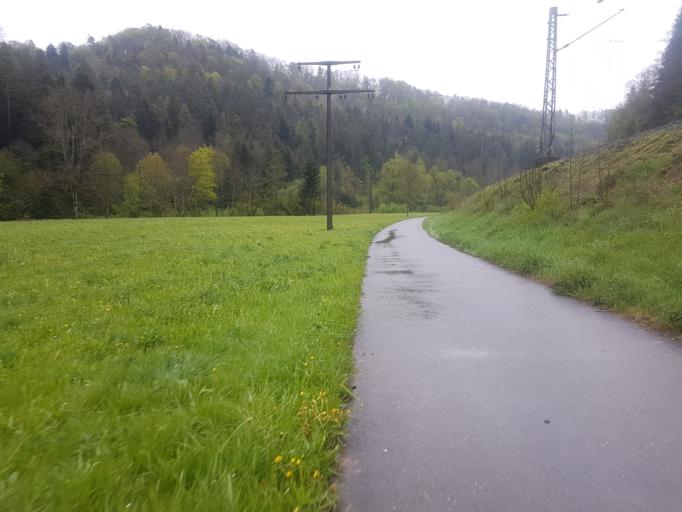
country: DE
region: Baden-Wuerttemberg
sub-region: Freiburg Region
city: Epfendorf
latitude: 48.2333
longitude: 8.6087
